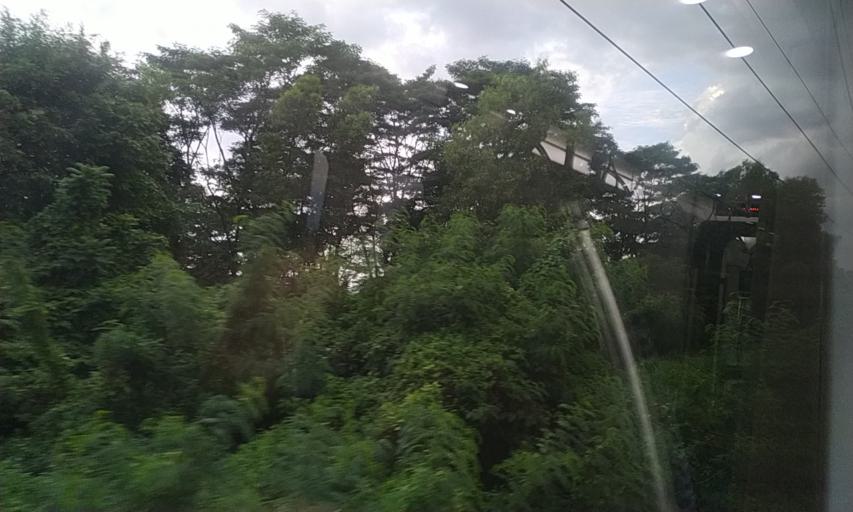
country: MY
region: Kuala Lumpur
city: Kuala Lumpur
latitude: 3.2270
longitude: 101.6728
